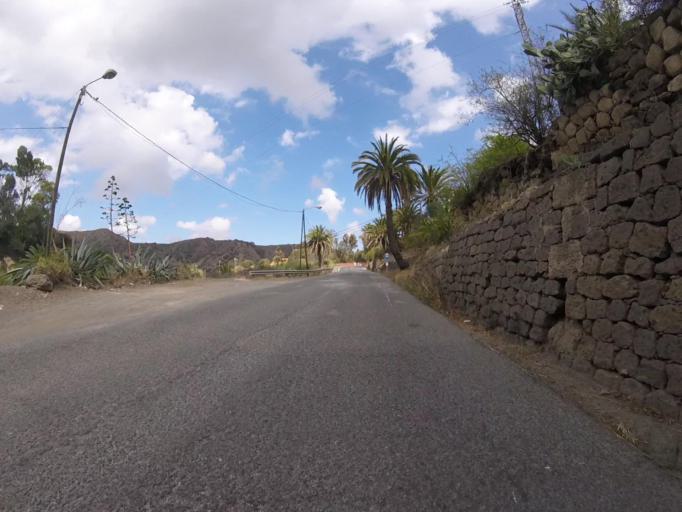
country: ES
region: Canary Islands
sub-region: Provincia de Las Palmas
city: Santa Brigida
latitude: 28.0576
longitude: -15.4651
